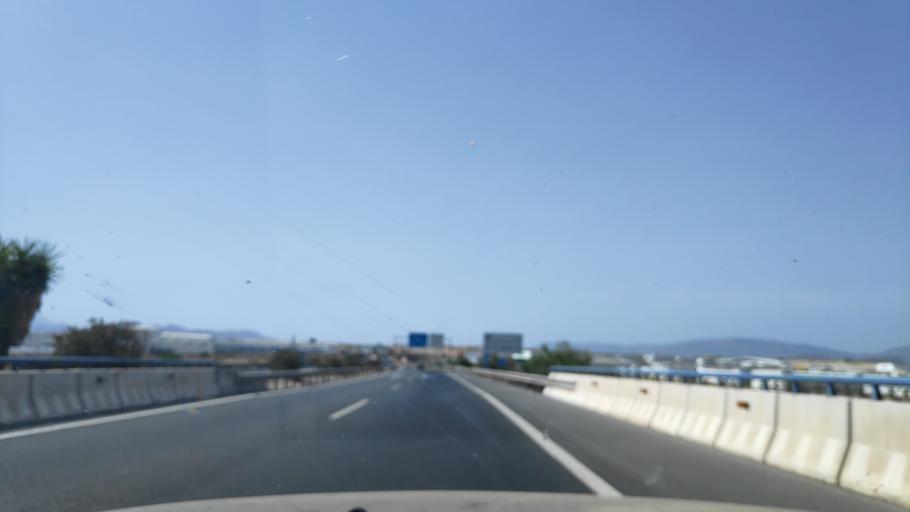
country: ES
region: Murcia
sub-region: Murcia
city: Lorqui
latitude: 38.0955
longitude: -1.2279
